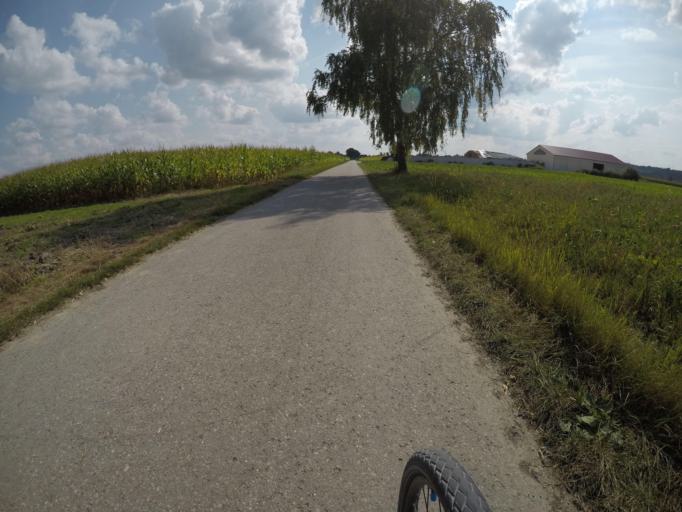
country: DE
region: Bavaria
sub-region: Swabia
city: Nordendorf
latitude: 48.5825
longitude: 10.8361
